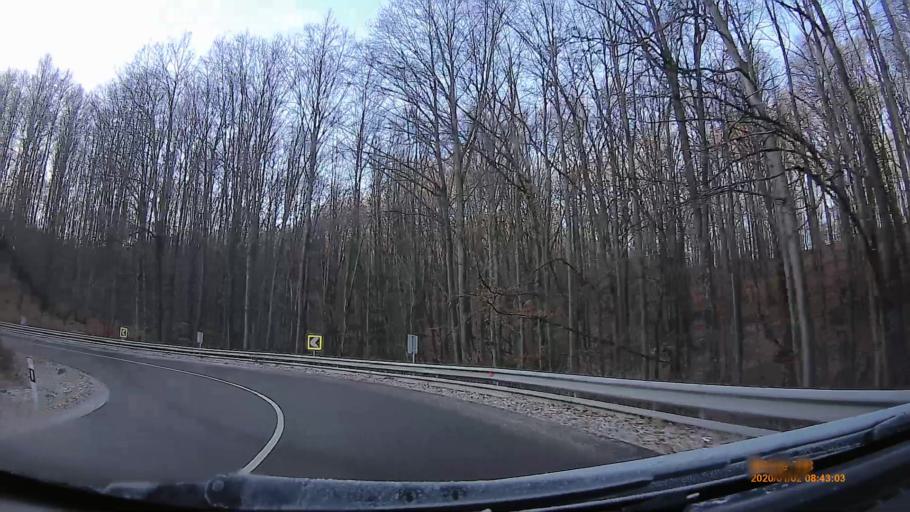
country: HU
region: Heves
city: Paradsasvar
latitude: 47.9070
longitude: 19.9858
